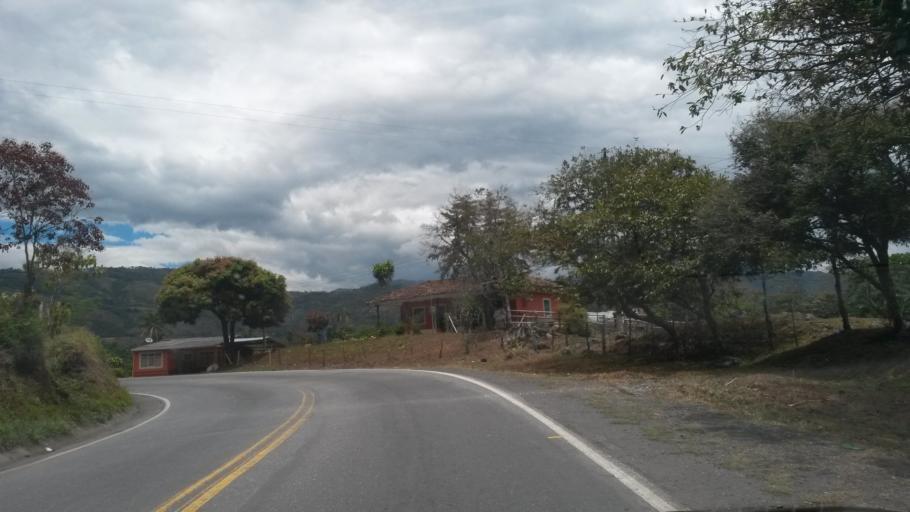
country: CO
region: Cauca
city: Rosas
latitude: 2.2539
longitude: -76.7596
